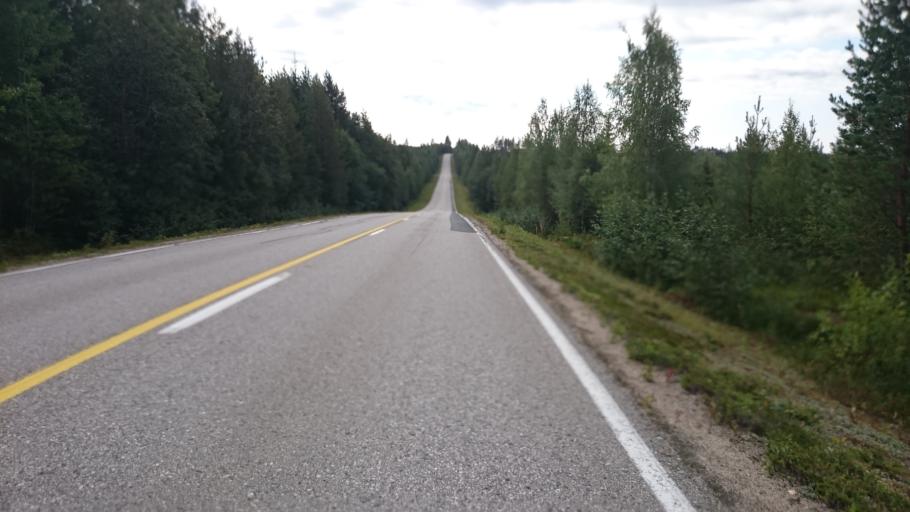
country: FI
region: Kainuu
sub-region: Kehys-Kainuu
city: Kuhmo
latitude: 64.4291
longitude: 29.8125
